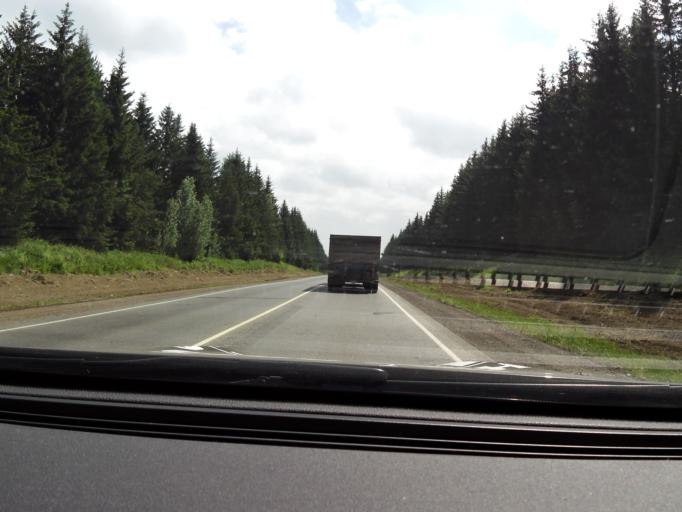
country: RU
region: Perm
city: Kukushtan
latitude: 57.5267
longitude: 56.6207
